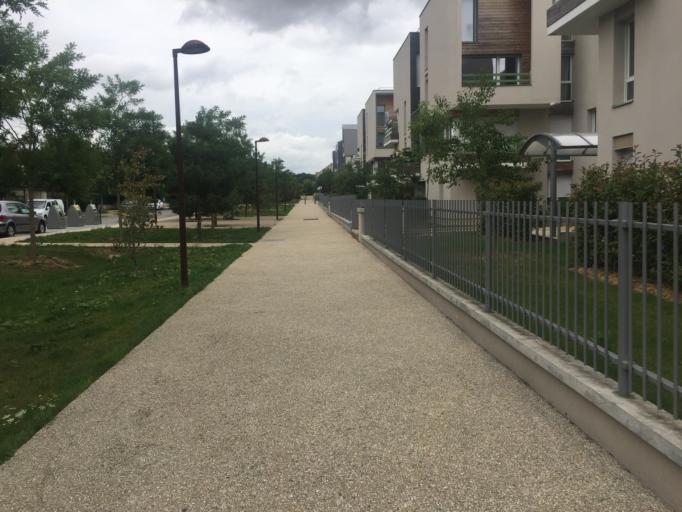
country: FR
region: Ile-de-France
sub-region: Departement des Yvelines
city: Bois-d'Arcy
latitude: 48.8044
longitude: 2.0117
